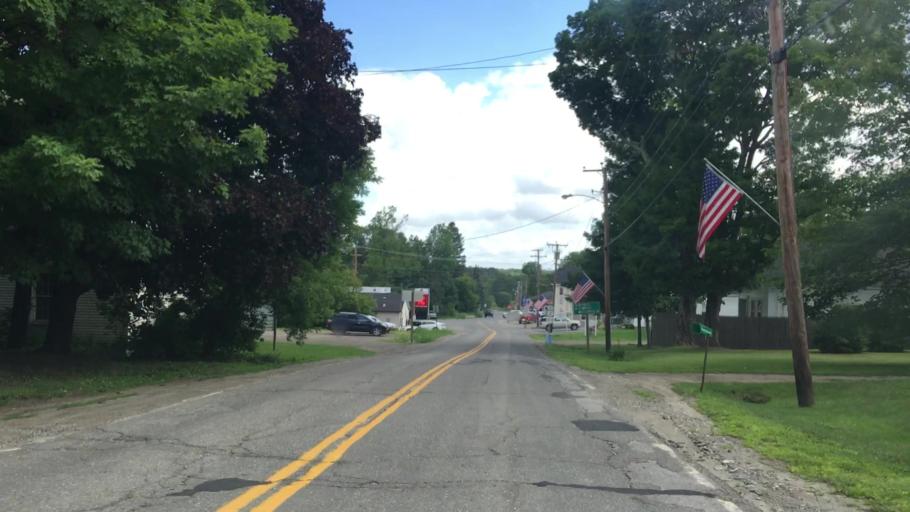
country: US
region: Maine
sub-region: Penobscot County
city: Carmel
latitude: 44.7967
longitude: -69.0531
